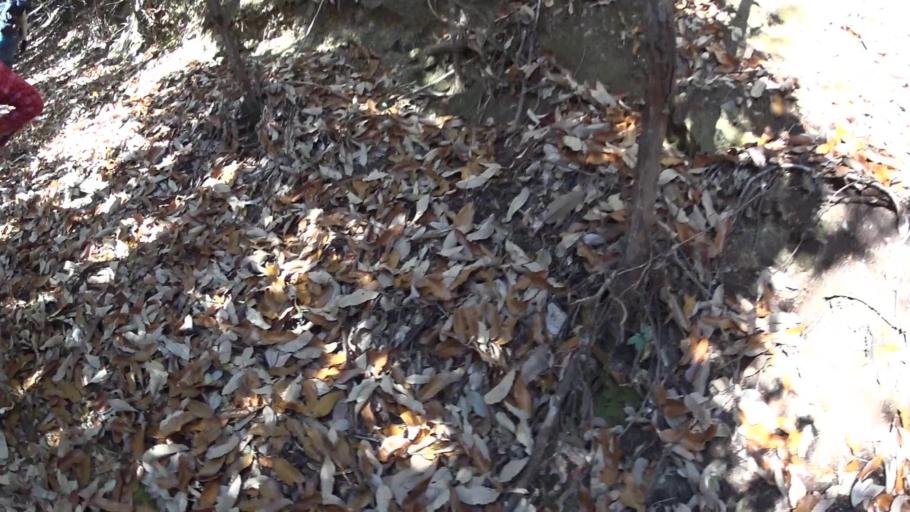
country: JP
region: Kyoto
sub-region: Kyoto-shi
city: Kamigyo-ku
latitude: 35.1006
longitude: 135.7575
